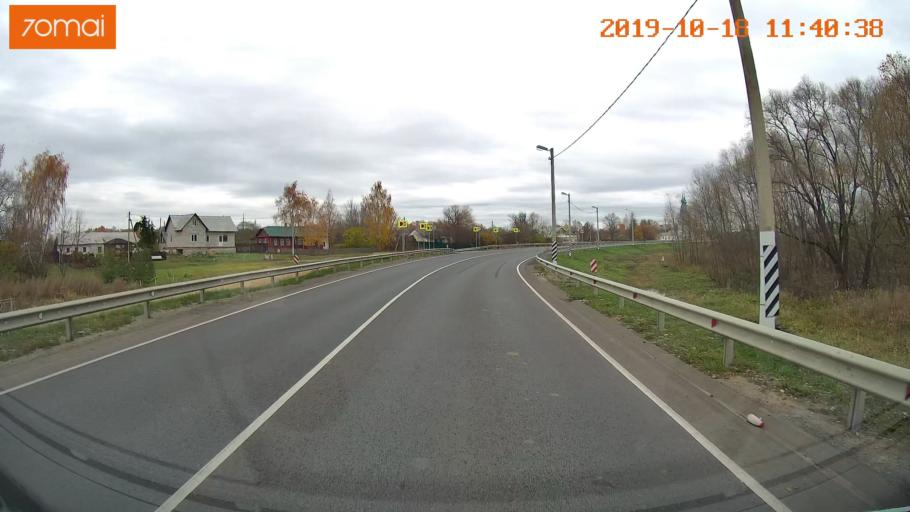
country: RU
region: Rjazan
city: Oktyabr'skiy
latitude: 54.1812
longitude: 38.8940
